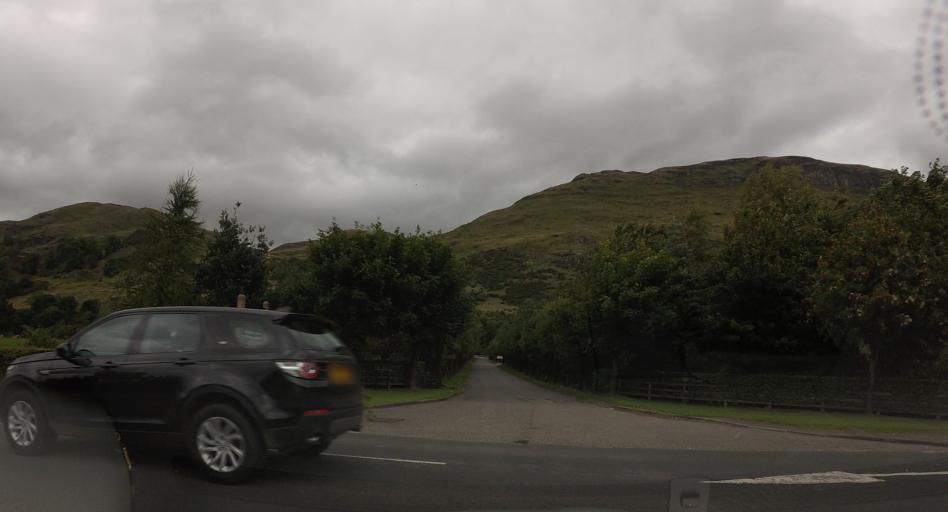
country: GB
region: Scotland
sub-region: Clackmannanshire
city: Alva
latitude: 56.1524
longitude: -3.8226
